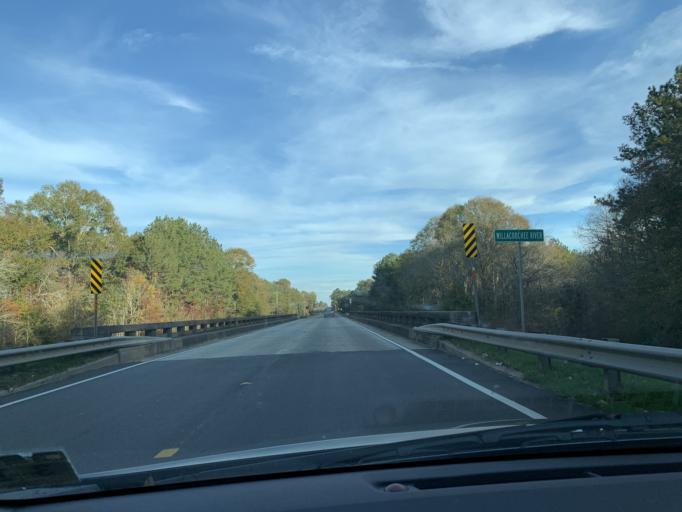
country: US
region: Georgia
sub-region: Irwin County
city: Ocilla
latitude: 31.5960
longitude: -83.1724
